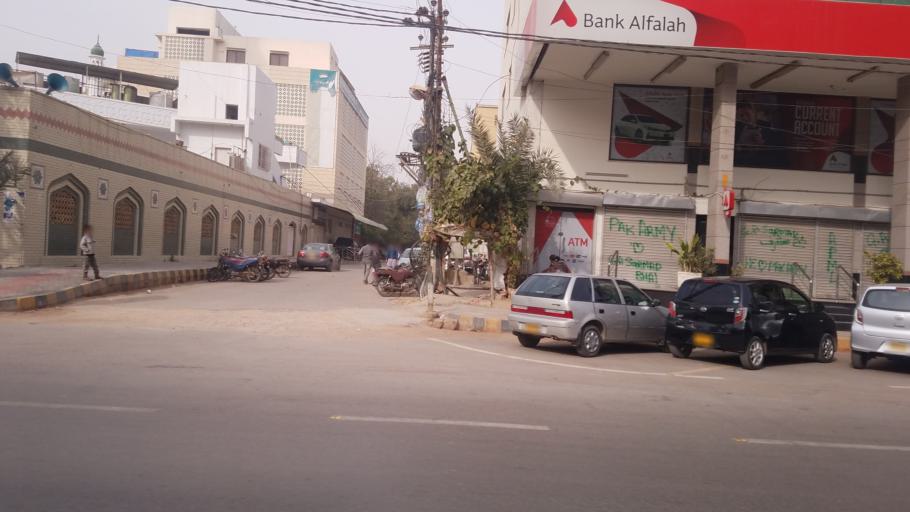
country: PK
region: Sindh
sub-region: Karachi District
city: Karachi
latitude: 24.8669
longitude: 67.0568
